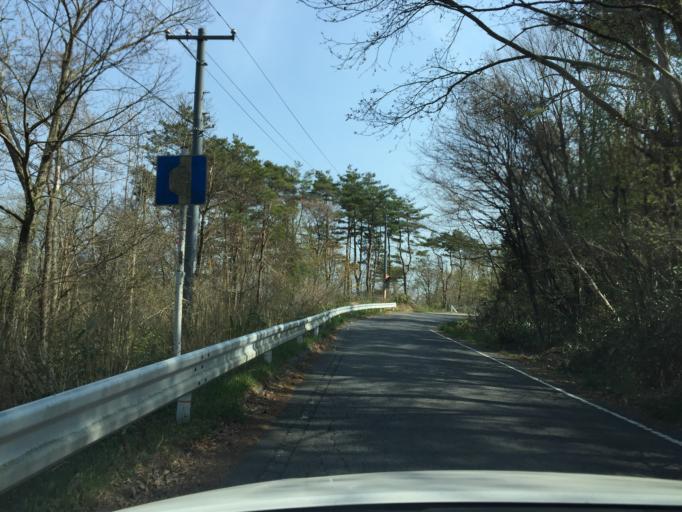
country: JP
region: Fukushima
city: Iwaki
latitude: 37.2075
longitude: 140.8580
